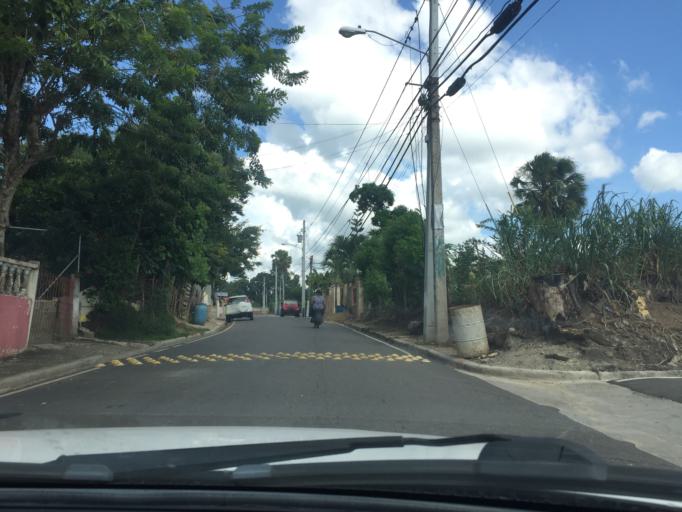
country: DO
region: Santiago
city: Licey al Medio
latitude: 19.3781
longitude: -70.6009
